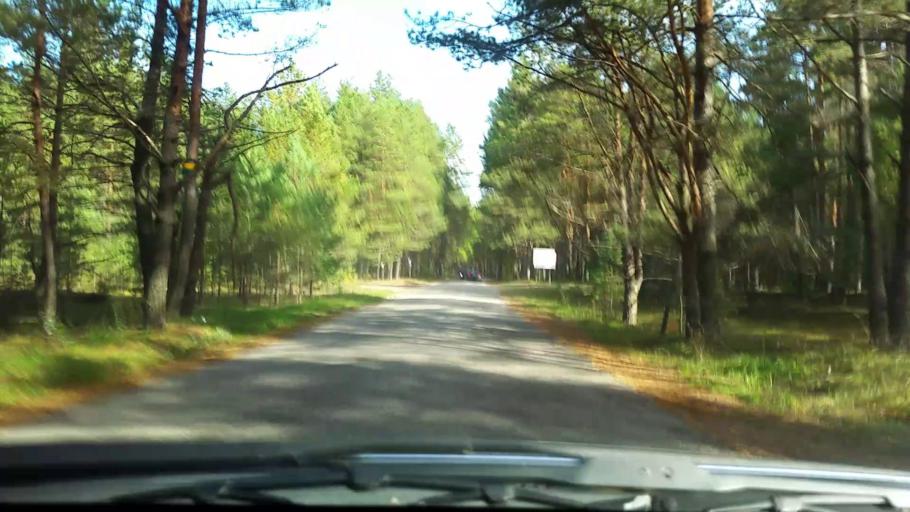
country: LV
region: Adazi
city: Adazi
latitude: 57.0994
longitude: 24.3731
